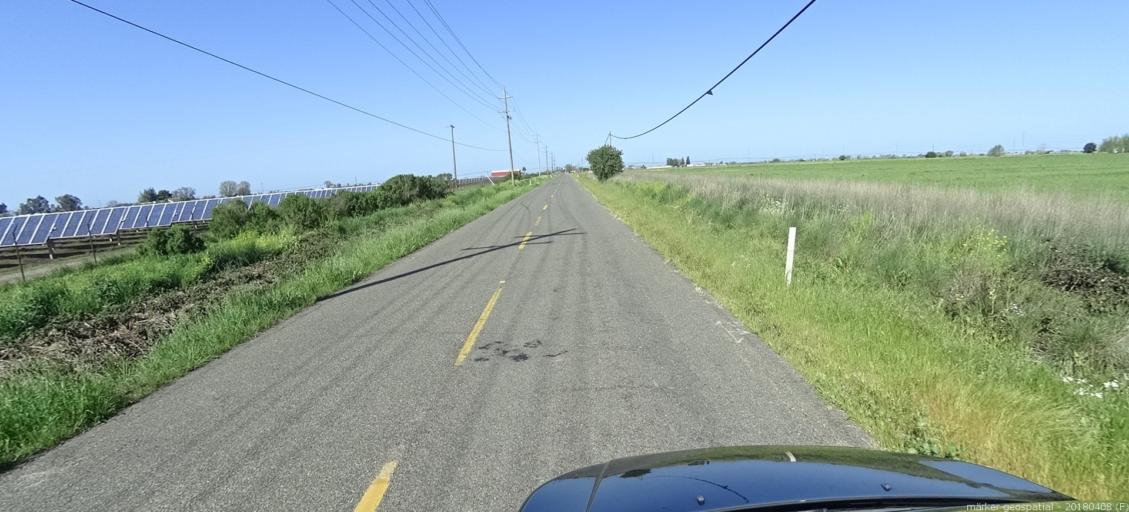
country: US
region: California
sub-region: Sacramento County
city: Elk Grove
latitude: 38.3505
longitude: -121.4119
